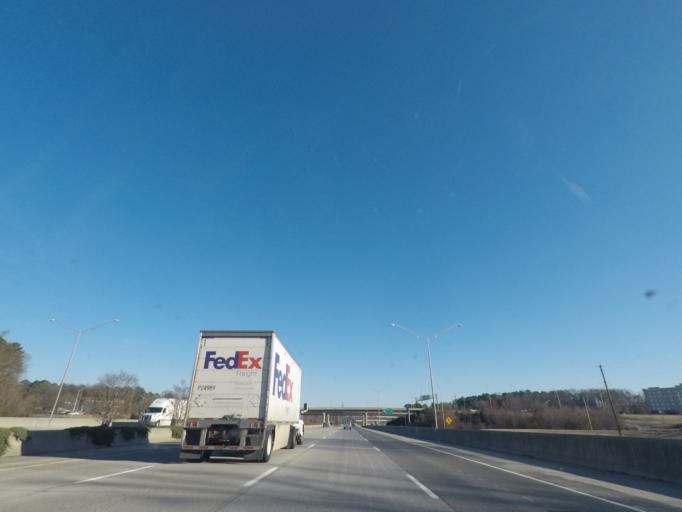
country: US
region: North Carolina
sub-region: Durham County
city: Durham
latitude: 36.0213
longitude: -78.9081
